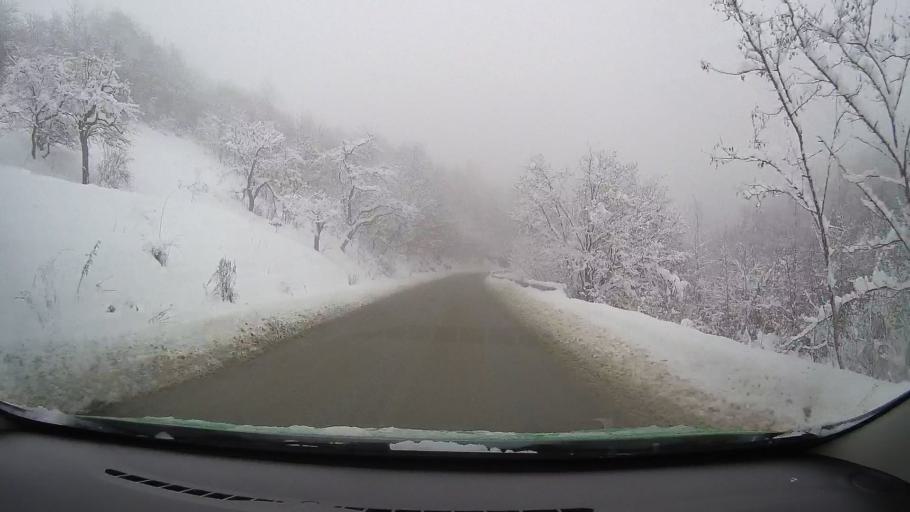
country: RO
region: Sibiu
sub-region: Comuna Poiana Sibiului
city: Poiana Sibiului
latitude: 45.7984
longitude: 23.7908
